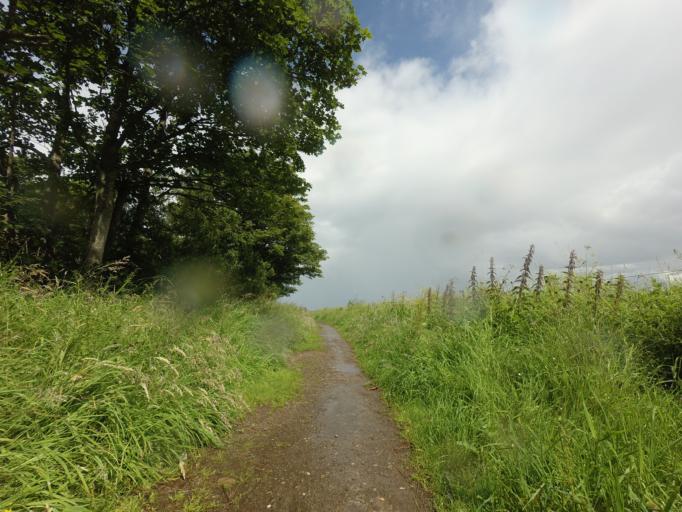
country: GB
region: Scotland
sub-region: Moray
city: Fochabers
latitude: 57.6684
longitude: -3.0909
